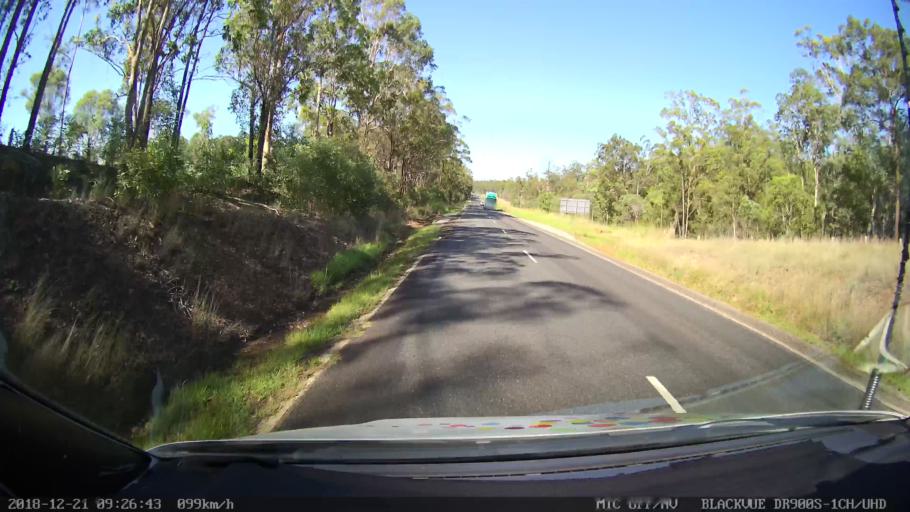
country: AU
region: New South Wales
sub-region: Clarence Valley
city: Maclean
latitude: -29.3959
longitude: 152.9987
